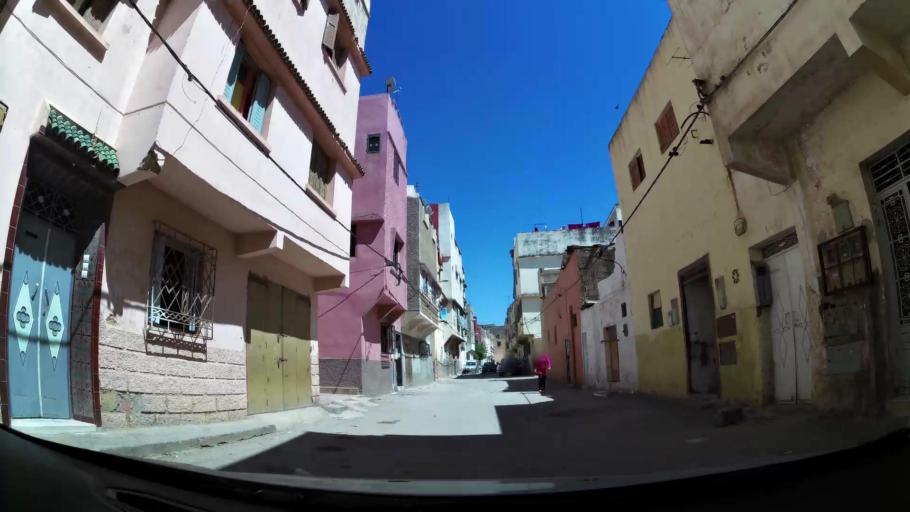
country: MA
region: Meknes-Tafilalet
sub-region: Meknes
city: Meknes
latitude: 33.8699
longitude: -5.5618
